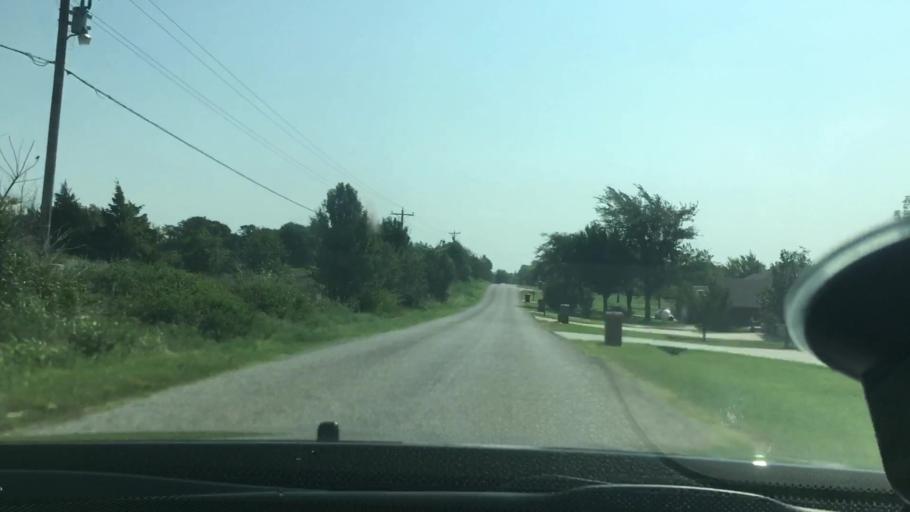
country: US
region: Oklahoma
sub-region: Bryan County
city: Durant
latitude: 34.0121
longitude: -96.4371
